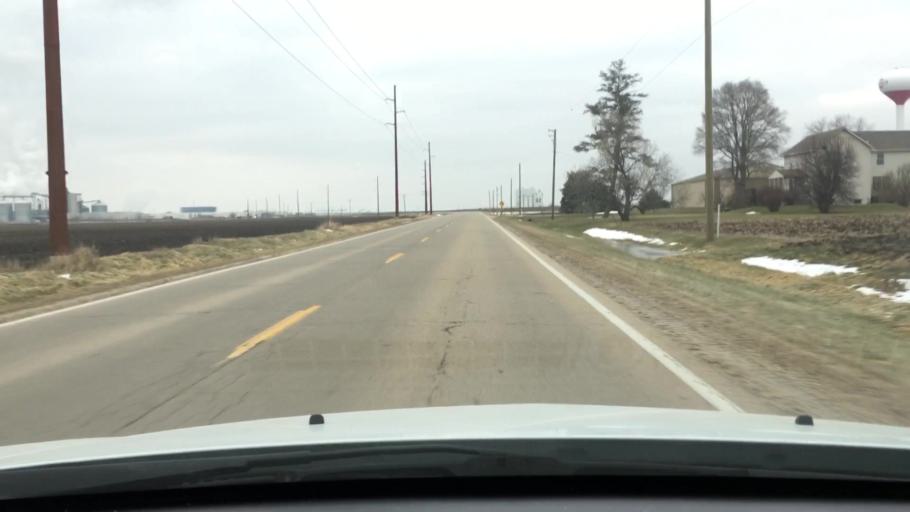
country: US
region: Illinois
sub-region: Ogle County
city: Rochelle
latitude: 41.8801
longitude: -89.0251
